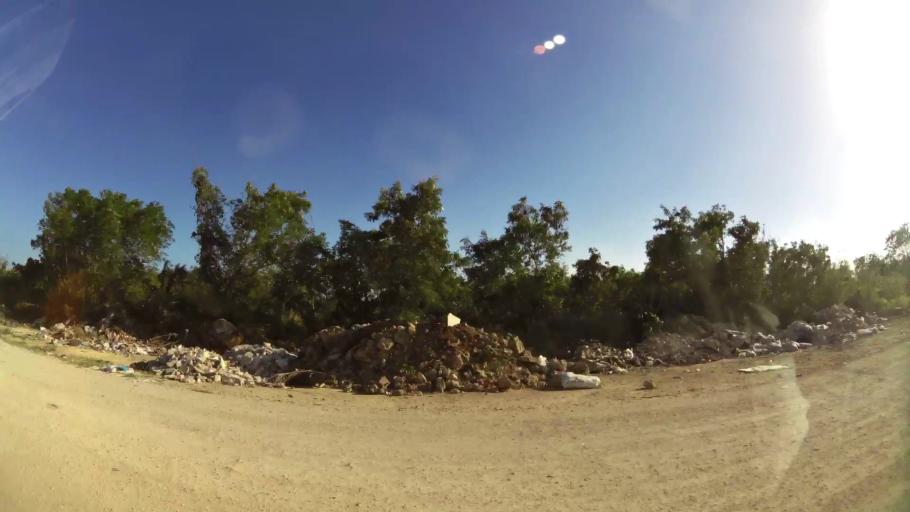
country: DO
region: Santo Domingo
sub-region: Santo Domingo
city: Santo Domingo Este
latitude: 18.4829
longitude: -69.8084
